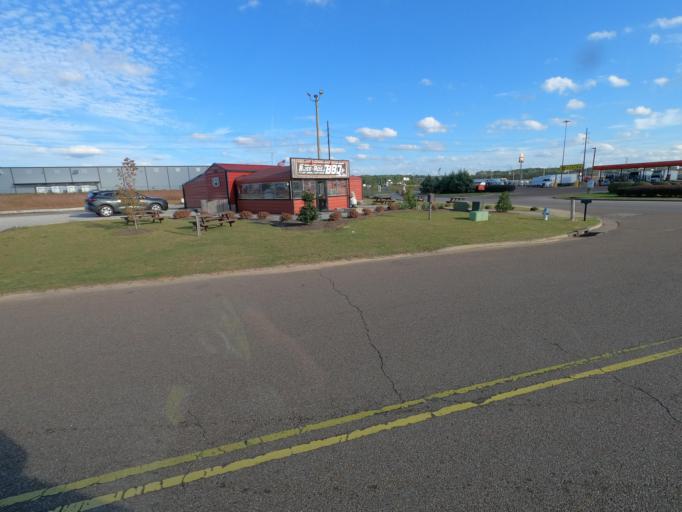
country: US
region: Tennessee
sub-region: Madison County
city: Jackson
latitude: 35.6839
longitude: -88.7775
